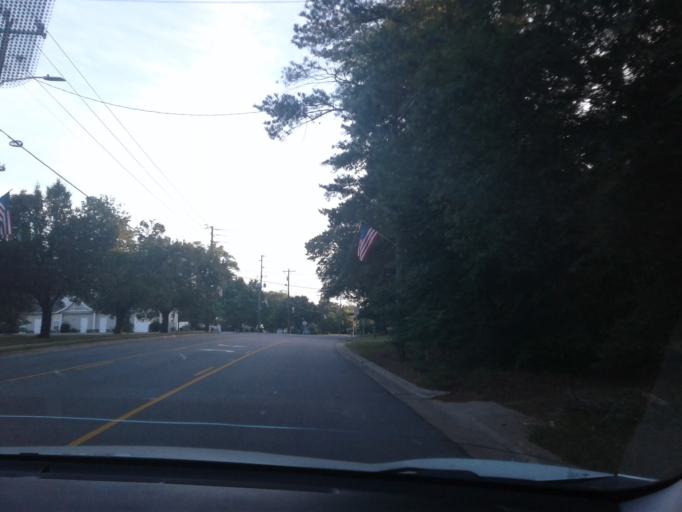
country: US
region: North Carolina
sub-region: Wake County
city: Fuquay-Varina
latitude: 35.5741
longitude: -78.8006
